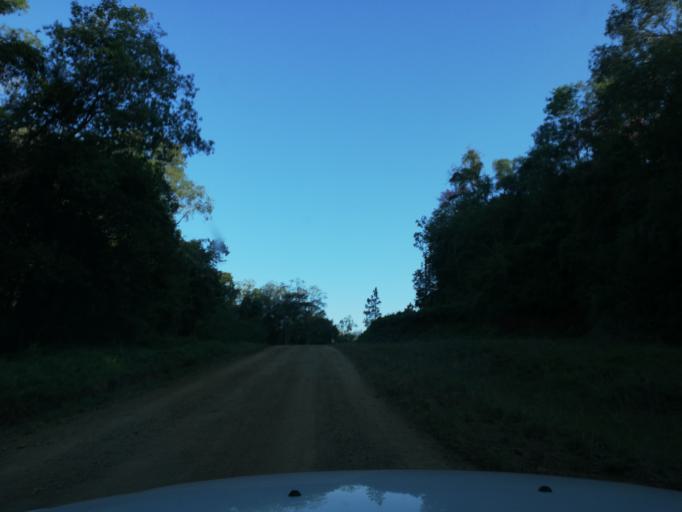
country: AR
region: Misiones
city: Cerro Cora
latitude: -27.6170
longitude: -55.7061
